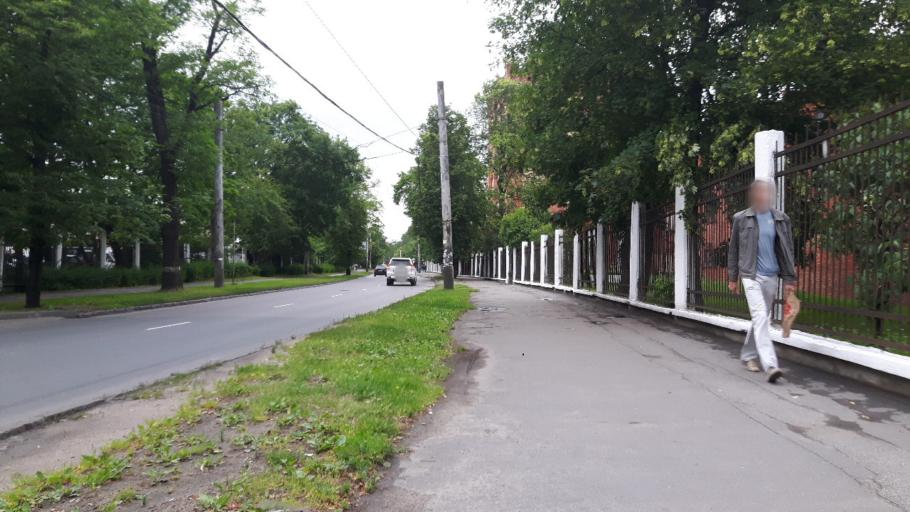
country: RU
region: Kaliningrad
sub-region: Gorod Kaliningrad
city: Kaliningrad
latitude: 54.7383
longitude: 20.4796
